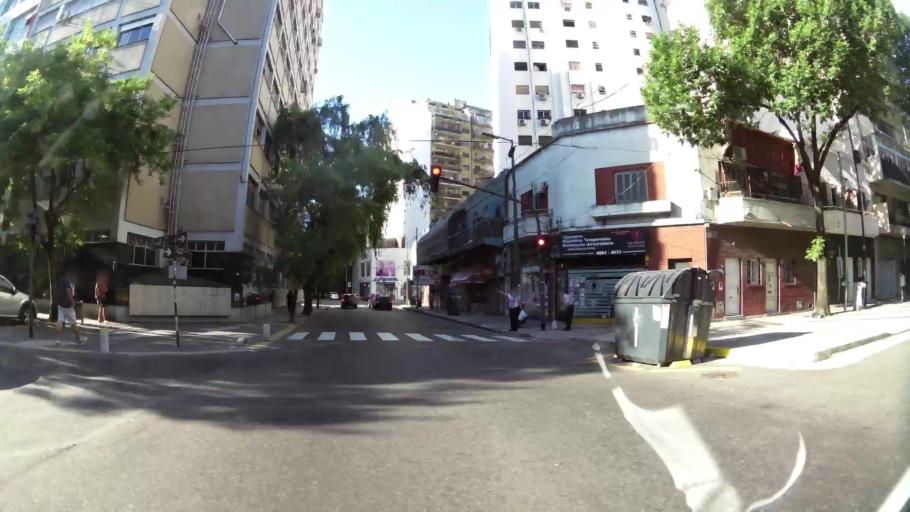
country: AR
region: Buenos Aires F.D.
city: Colegiales
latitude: -34.6149
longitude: -58.4274
